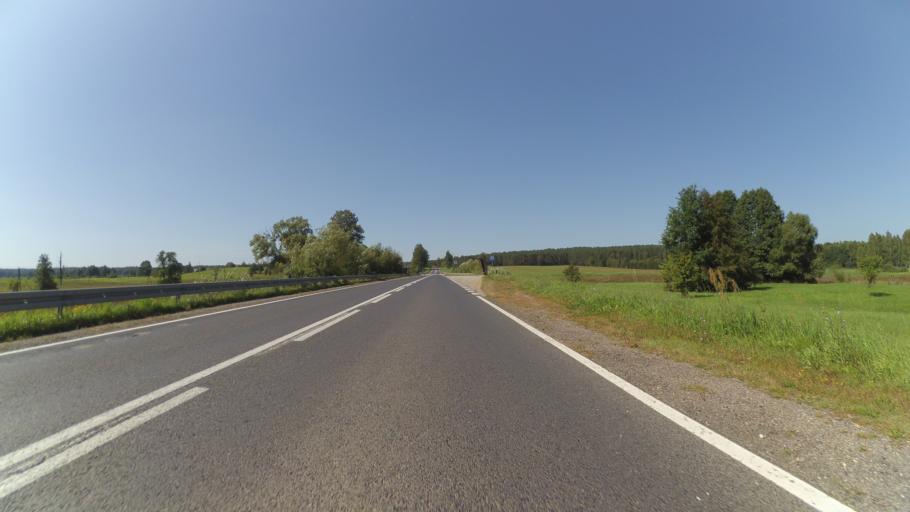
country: PL
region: Podlasie
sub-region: Powiat bialostocki
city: Suprasl
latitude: 53.1404
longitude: 23.4702
